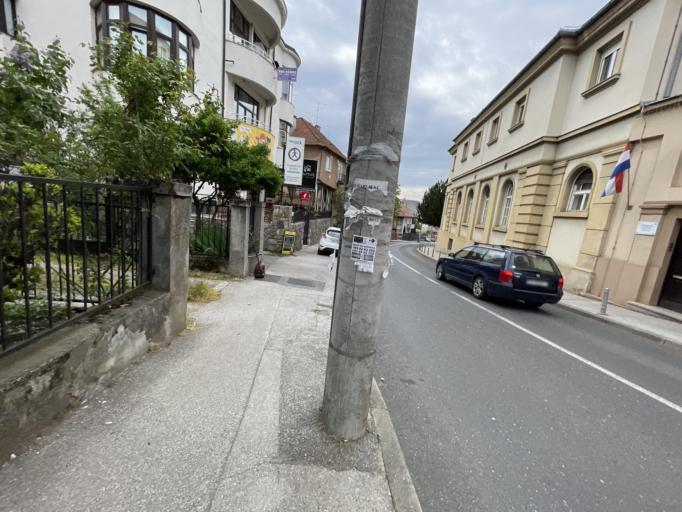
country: HR
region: Grad Zagreb
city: Zagreb - Centar
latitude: 45.8169
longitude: 15.9414
